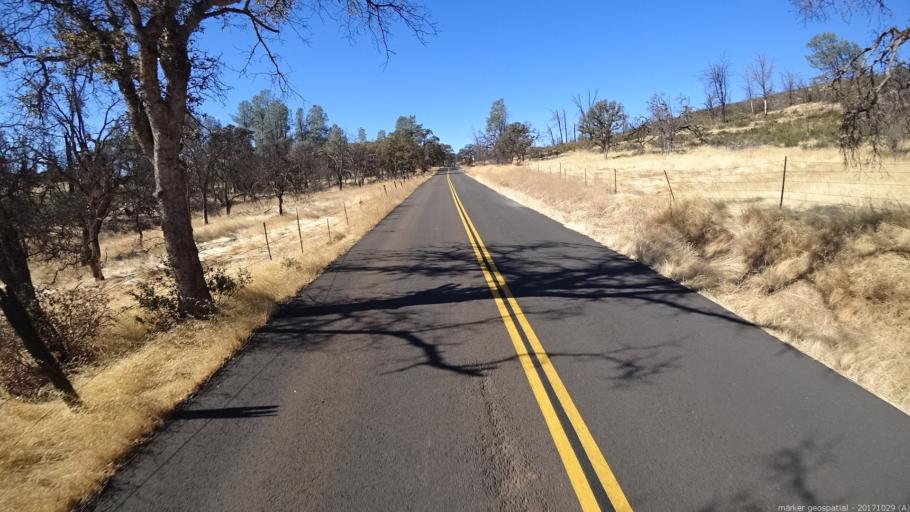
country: US
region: California
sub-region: Trinity County
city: Lewiston
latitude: 40.4241
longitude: -122.7605
